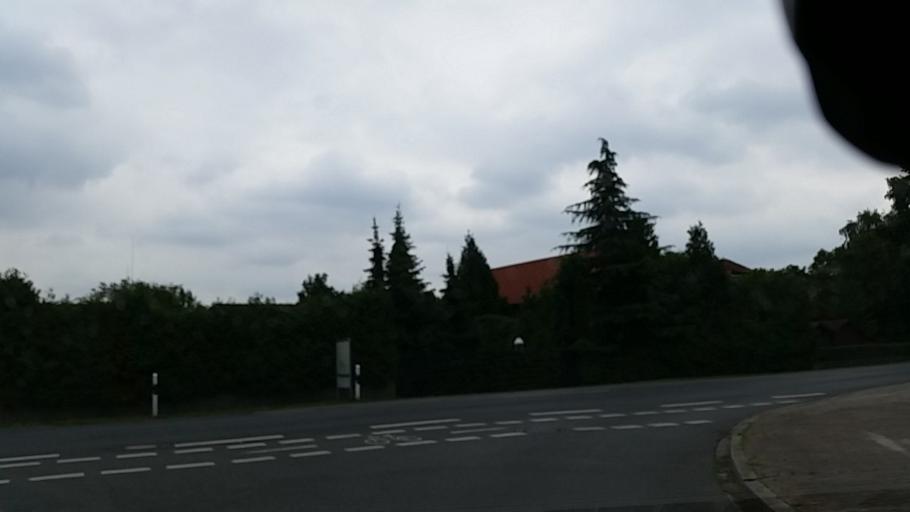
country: DE
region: Lower Saxony
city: Ruhen
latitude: 52.4536
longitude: 10.8518
